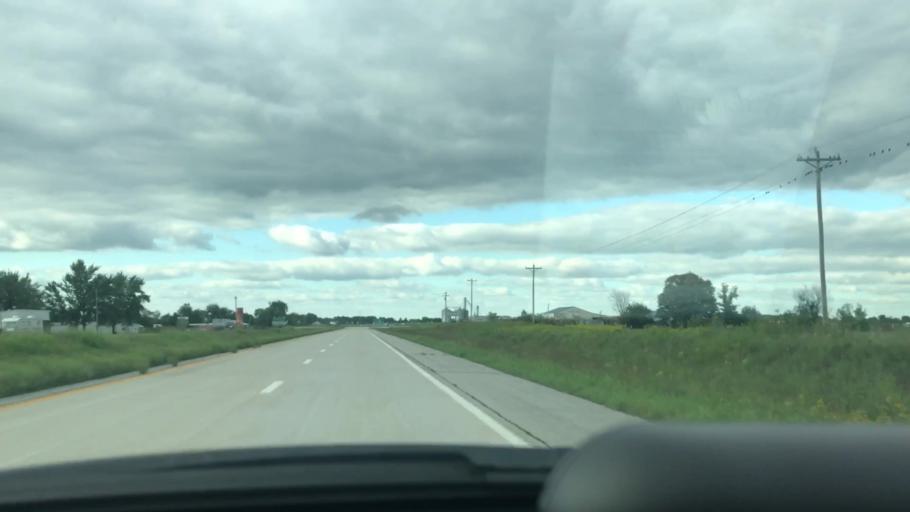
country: US
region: Missouri
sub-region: Benton County
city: Lincoln
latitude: 38.3710
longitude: -93.3386
